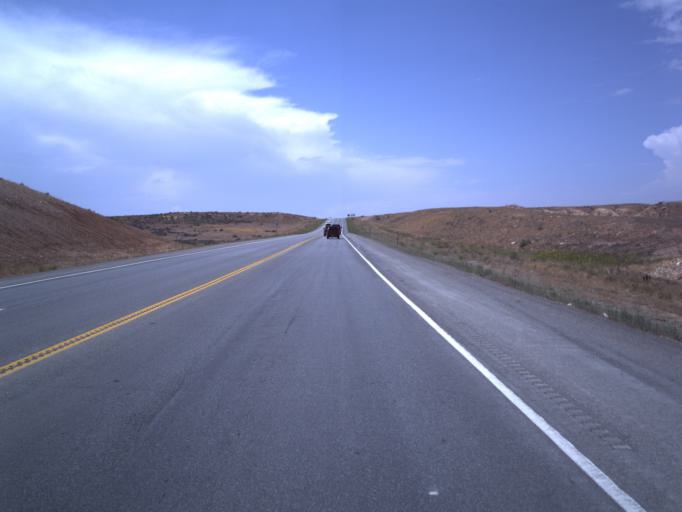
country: US
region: Utah
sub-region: Uintah County
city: Maeser
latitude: 40.3362
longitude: -109.6376
